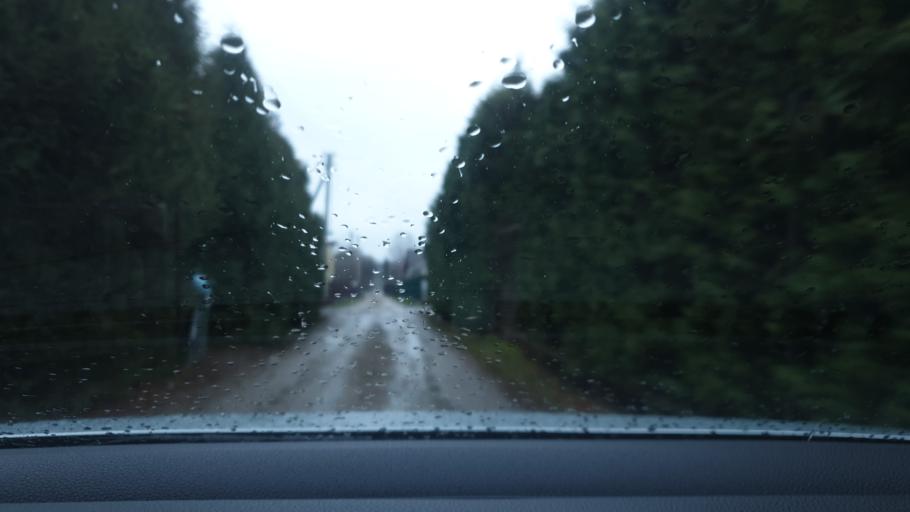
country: LT
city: Skaidiskes
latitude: 54.7058
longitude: 25.4069
